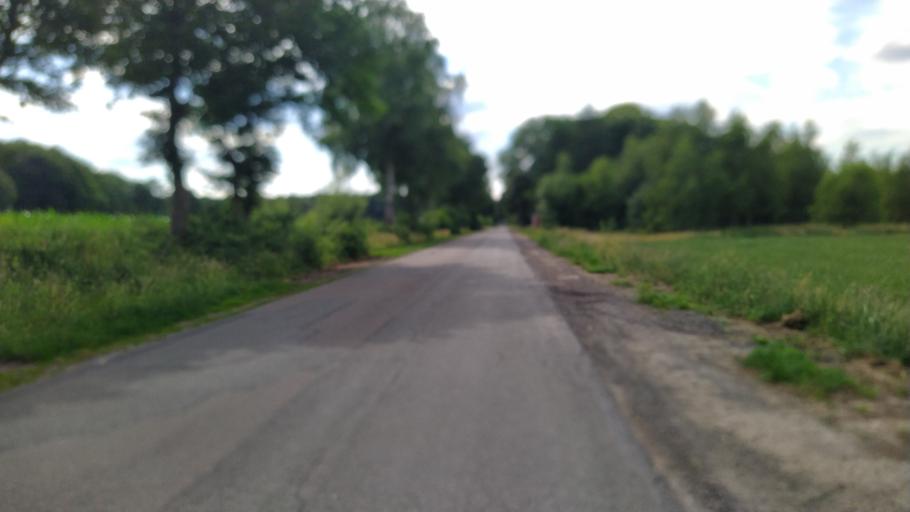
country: DE
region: Lower Saxony
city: Armstorf
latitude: 53.6061
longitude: 9.0560
